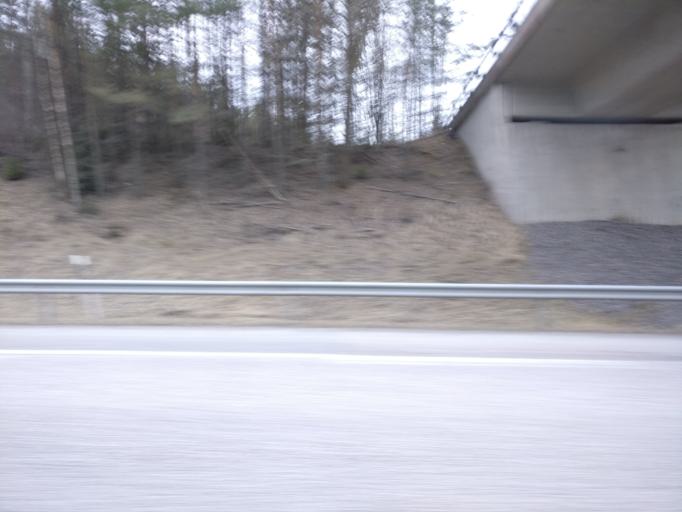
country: FI
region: Uusimaa
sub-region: Helsinki
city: Hyvinge
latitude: 60.5716
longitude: 24.8140
